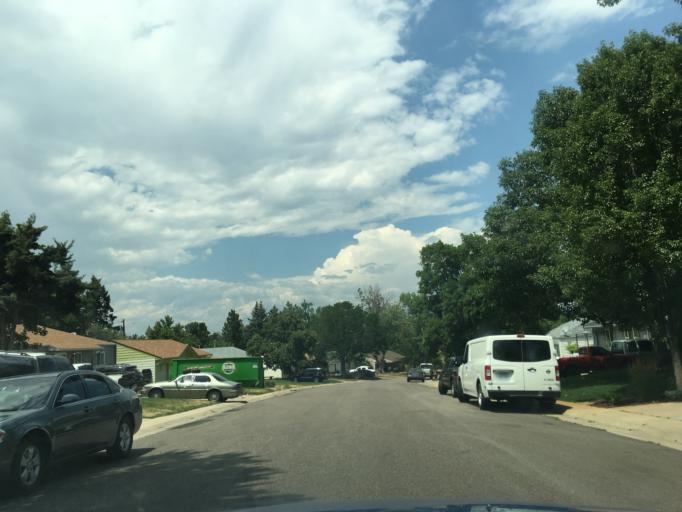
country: US
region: Colorado
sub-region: Arapahoe County
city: Sheridan
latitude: 39.6835
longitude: -105.0366
